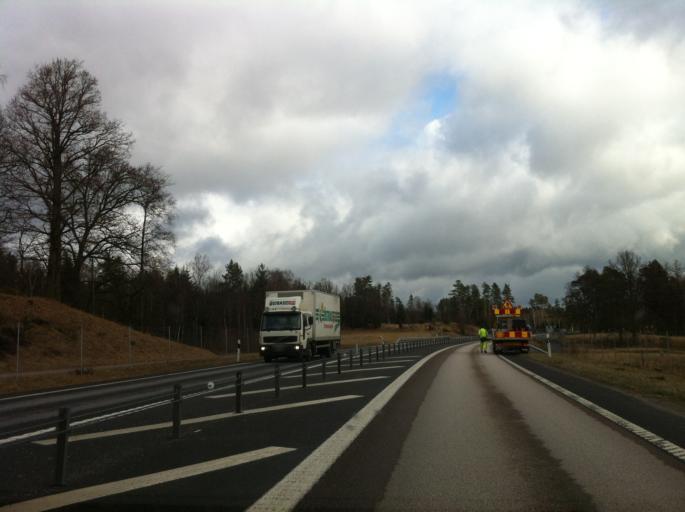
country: SE
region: Halland
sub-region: Halmstads Kommun
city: Oskarstrom
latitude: 56.8492
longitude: 13.0223
